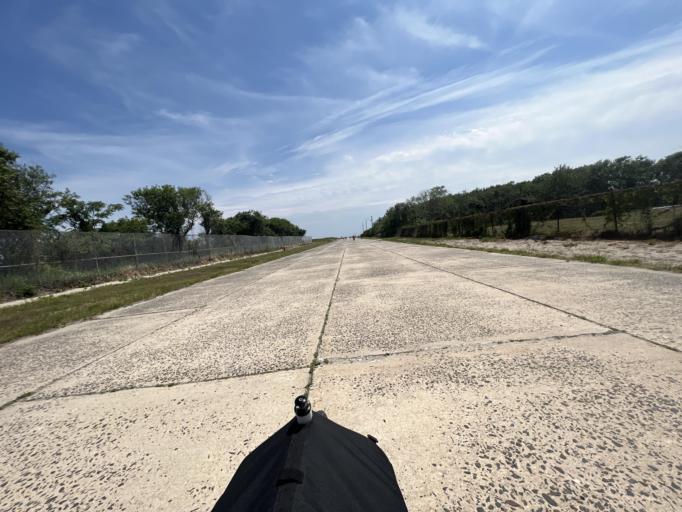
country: US
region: New York
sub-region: Kings County
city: East New York
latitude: 40.5647
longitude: -73.8811
